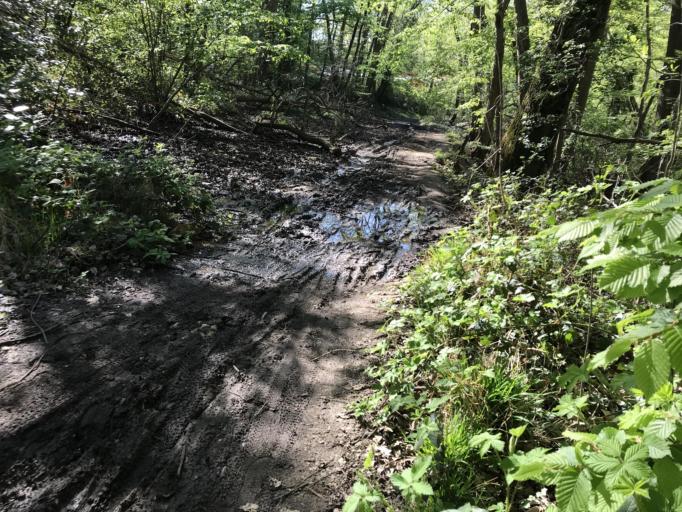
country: FR
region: Ile-de-France
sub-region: Departement de l'Essonne
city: Villejust
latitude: 48.6898
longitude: 2.2365
